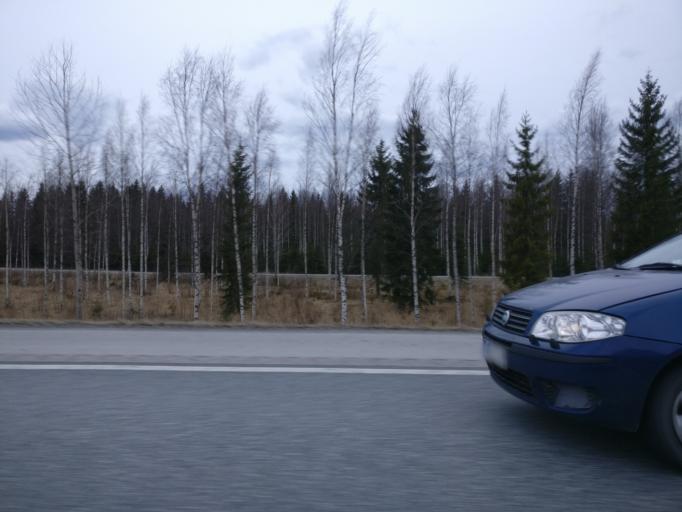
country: FI
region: Haeme
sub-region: Riihimaeki
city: Riihimaeki
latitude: 60.7531
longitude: 24.7295
